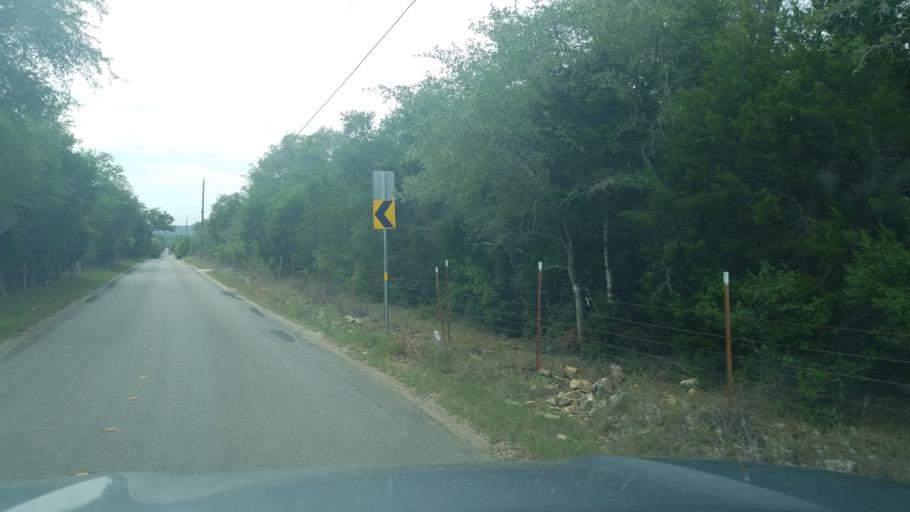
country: US
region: Texas
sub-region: Comal County
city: Bulverde
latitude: 29.7591
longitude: -98.4111
